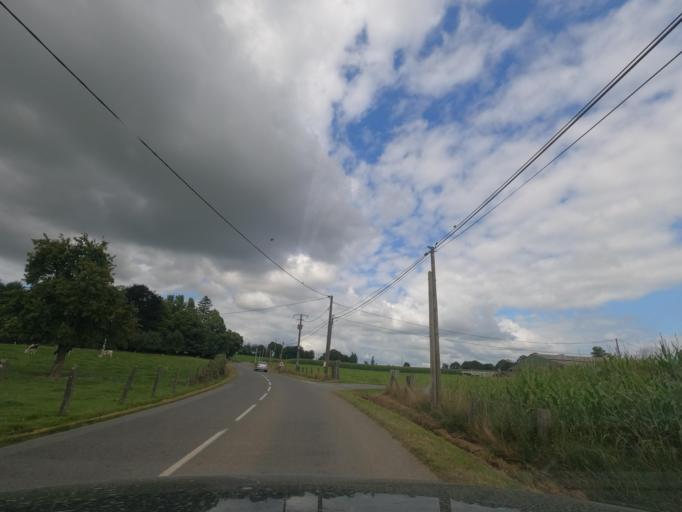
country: FR
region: Lower Normandy
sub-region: Departement de la Manche
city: Le Teilleul
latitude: 48.5238
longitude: -0.8881
